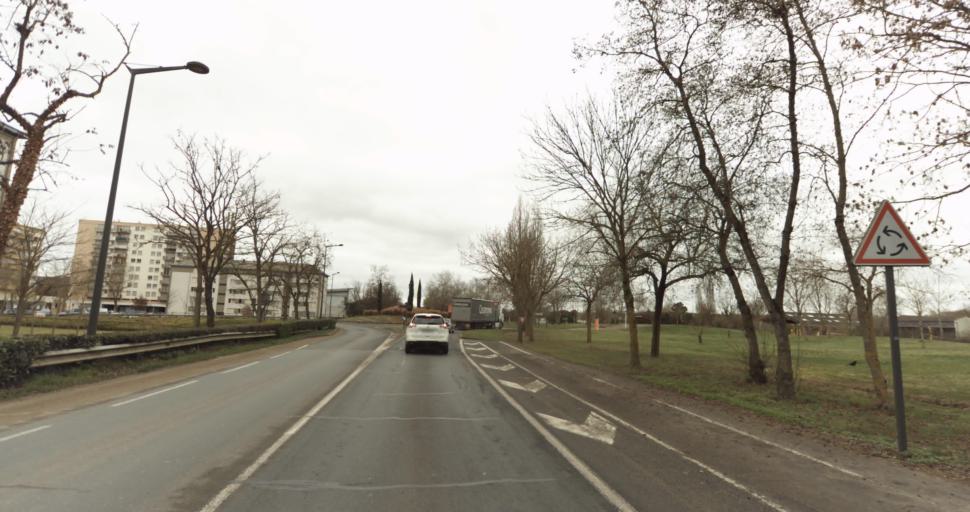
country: FR
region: Pays de la Loire
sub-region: Departement de Maine-et-Loire
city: Saumur
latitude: 47.2478
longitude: -0.0791
